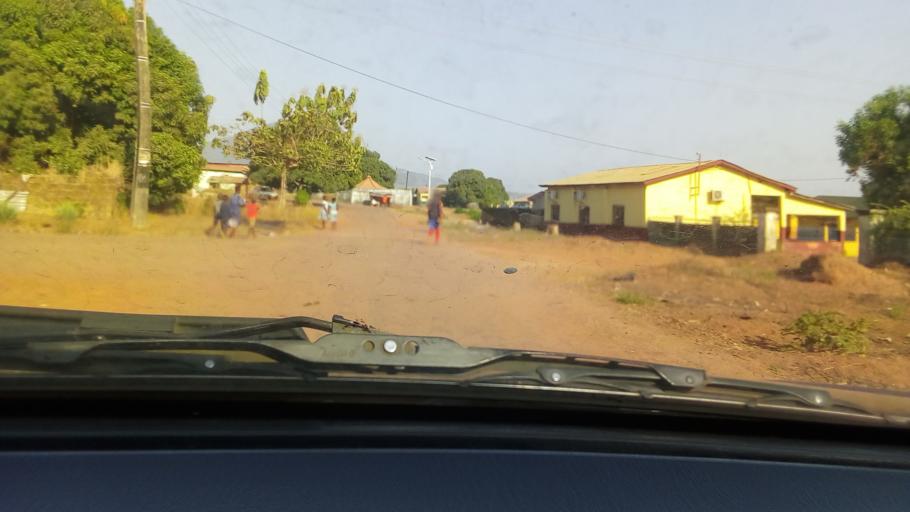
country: GN
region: Kindia
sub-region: Prefecture de Dubreka
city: Dubreka
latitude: 9.7874
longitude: -13.5236
